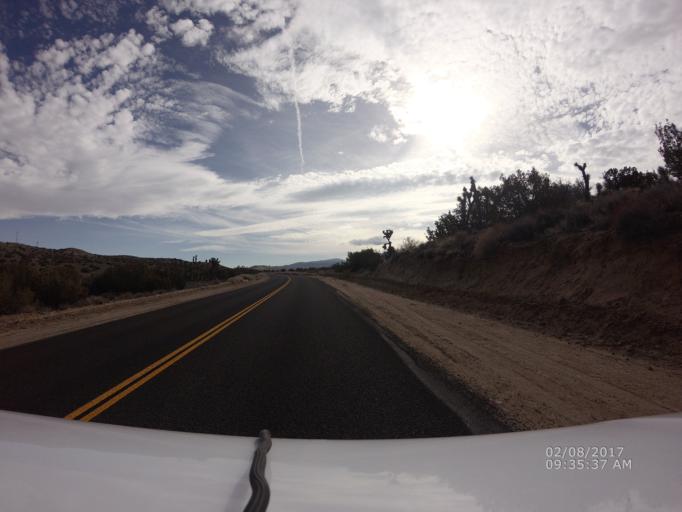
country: US
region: California
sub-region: Los Angeles County
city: Littlerock
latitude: 34.4653
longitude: -117.8878
